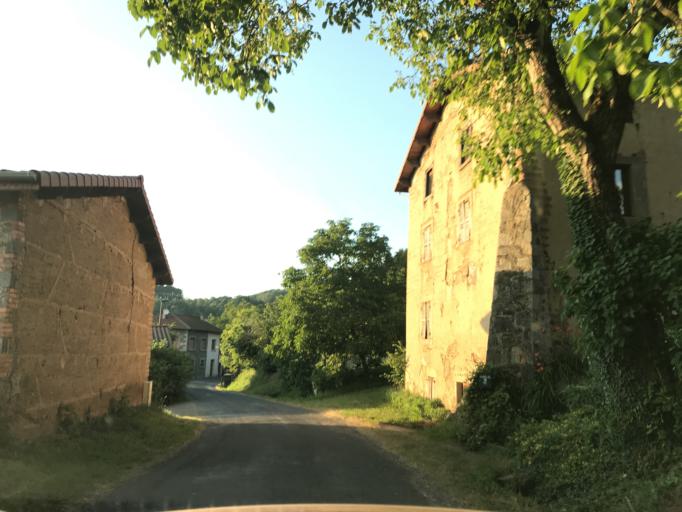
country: FR
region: Auvergne
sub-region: Departement du Puy-de-Dome
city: Courpiere
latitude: 45.7513
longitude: 3.6200
